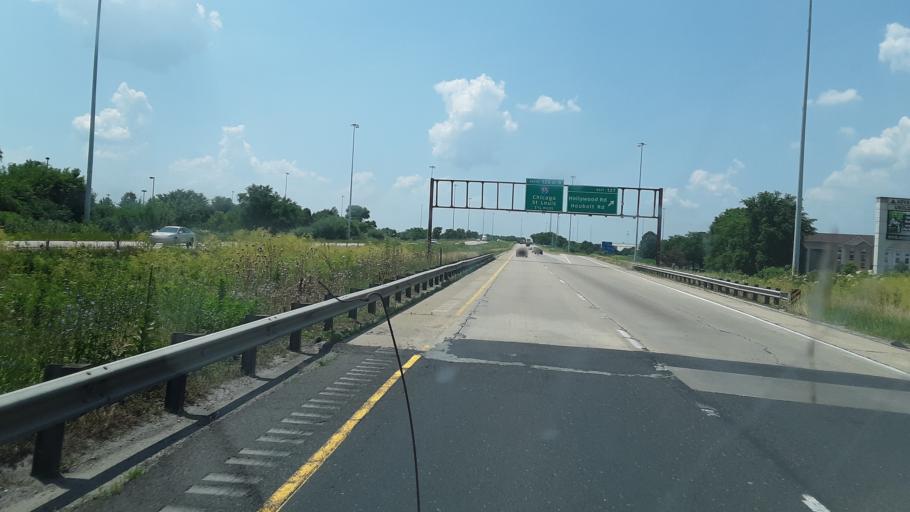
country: US
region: Illinois
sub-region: Will County
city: Shorewood
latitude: 41.4957
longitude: -88.1630
